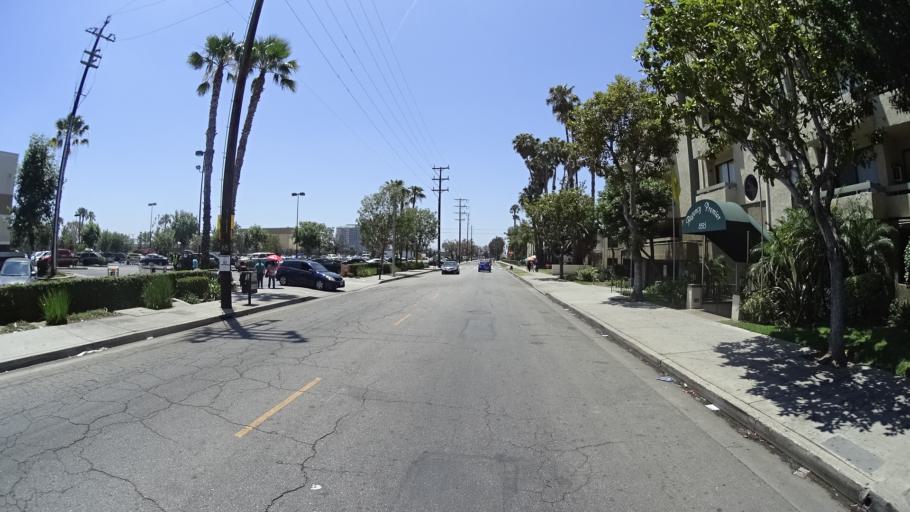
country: US
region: California
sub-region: Los Angeles County
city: Van Nuys
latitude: 34.2256
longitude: -118.4517
